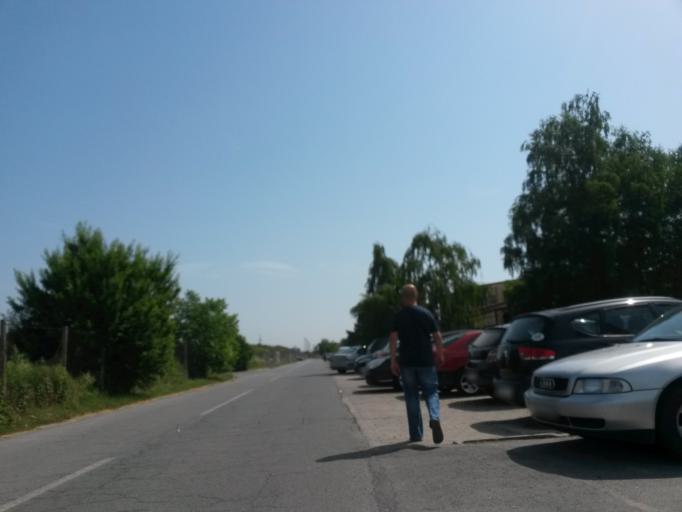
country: HR
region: Osjecko-Baranjska
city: Brijest
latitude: 45.5431
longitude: 18.6597
